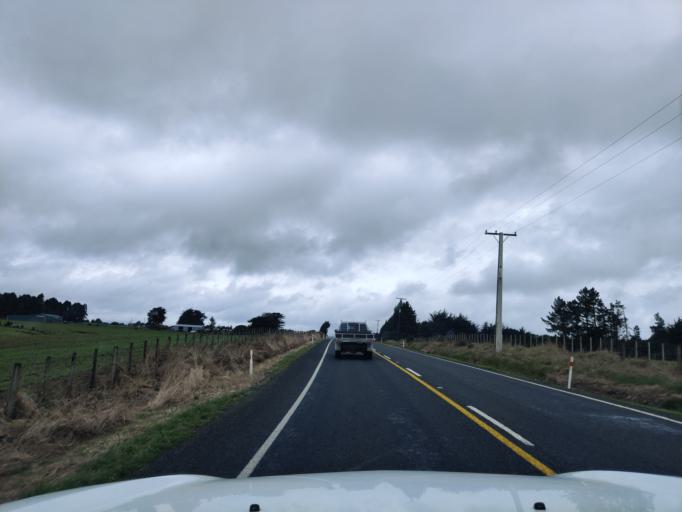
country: NZ
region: Manawatu-Wanganui
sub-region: Ruapehu District
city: Waiouru
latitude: -39.3631
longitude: 175.3431
